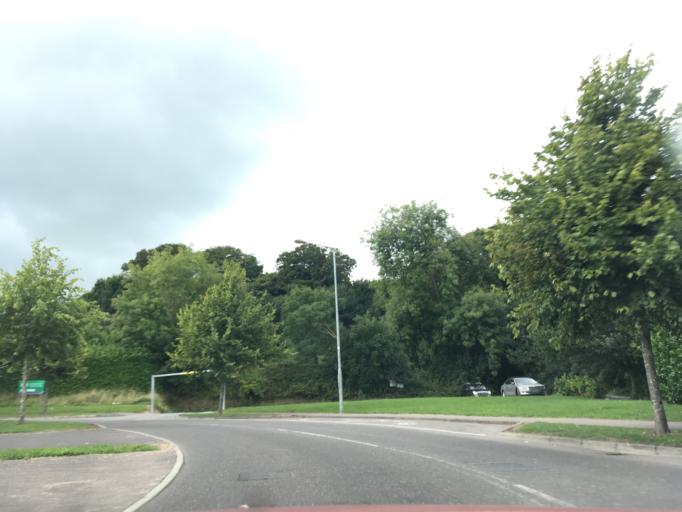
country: IE
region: Munster
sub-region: County Cork
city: Crosshaven
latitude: 51.7994
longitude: -8.2946
